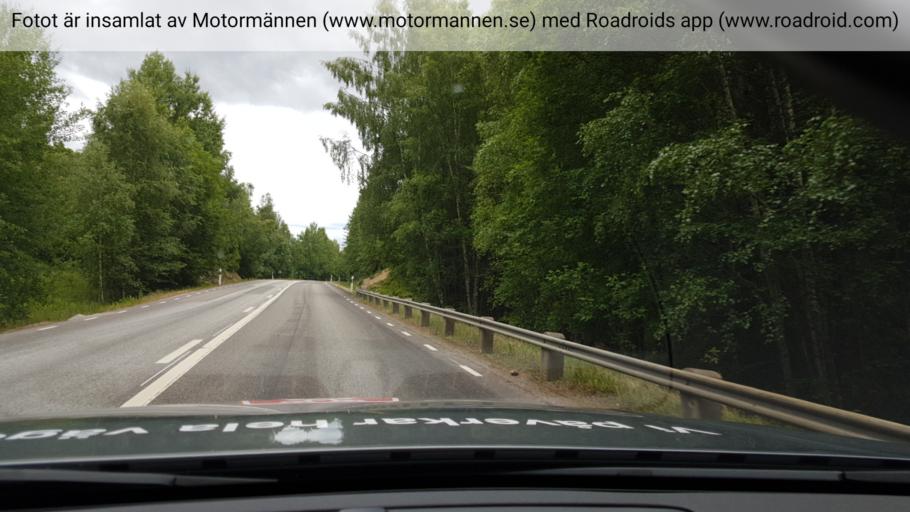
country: SE
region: Vaestmanland
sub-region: Skinnskattebergs Kommun
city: Skinnskatteberg
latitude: 59.8614
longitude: 15.6540
